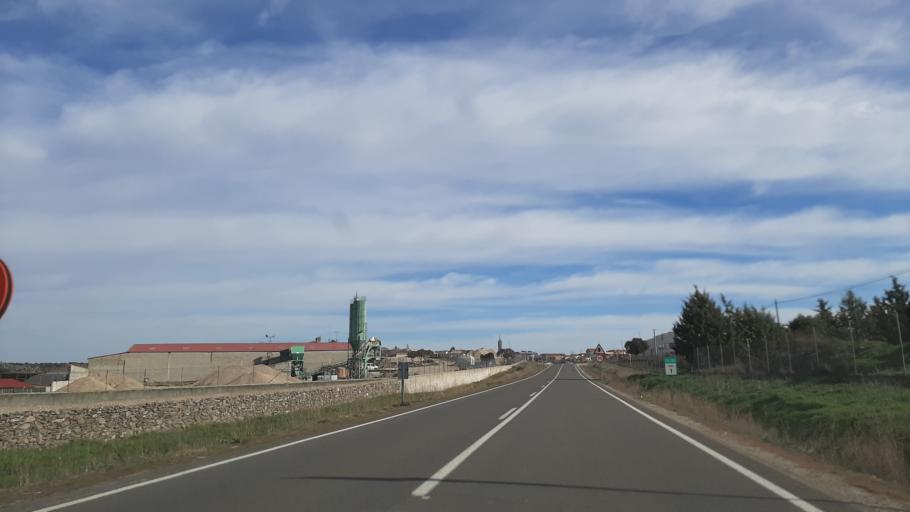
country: ES
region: Castille and Leon
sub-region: Provincia de Salamanca
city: Ledesma
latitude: 41.0924
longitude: -6.0157
